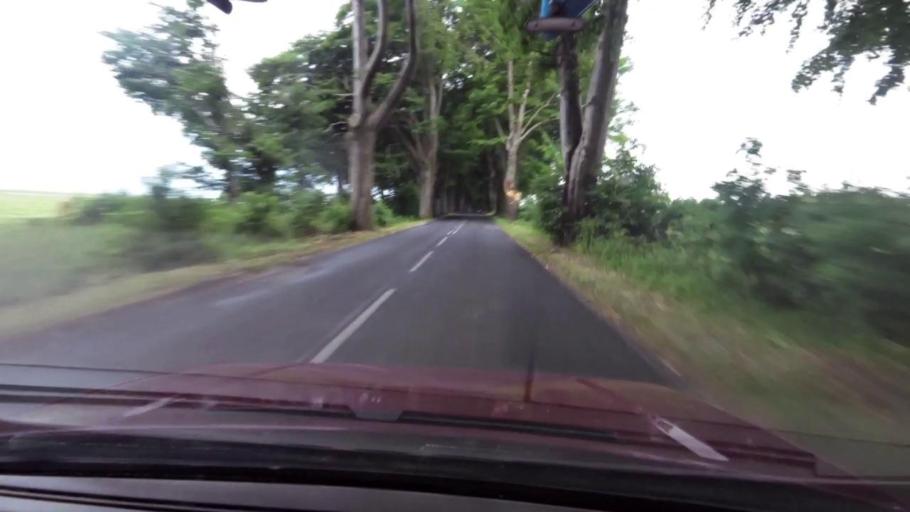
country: PL
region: West Pomeranian Voivodeship
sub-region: Powiat koszalinski
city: Polanow
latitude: 54.1413
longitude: 16.5443
